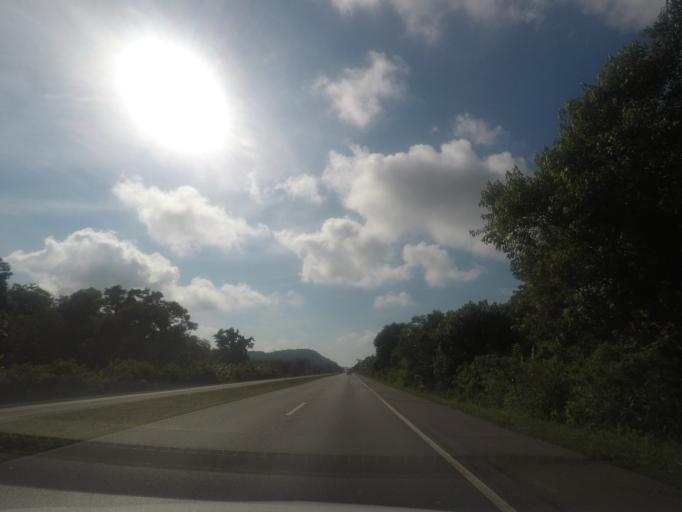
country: BR
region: Parana
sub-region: Antonina
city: Antonina
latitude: -25.5390
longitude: -48.7728
